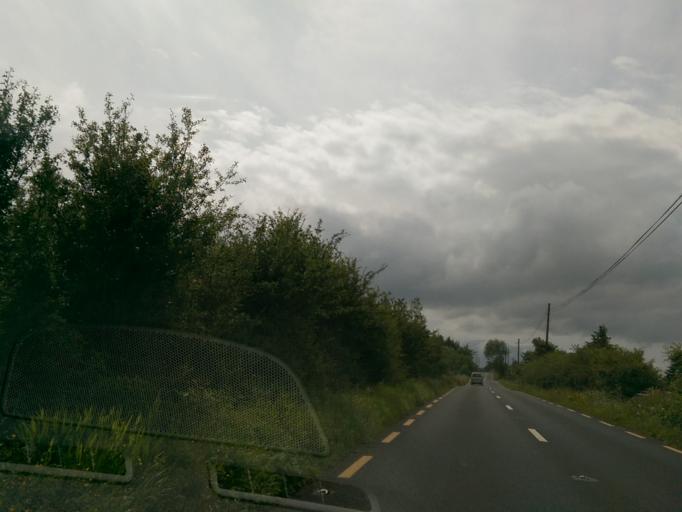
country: IE
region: Munster
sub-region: An Clar
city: Kilrush
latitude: 52.6933
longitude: -9.3457
